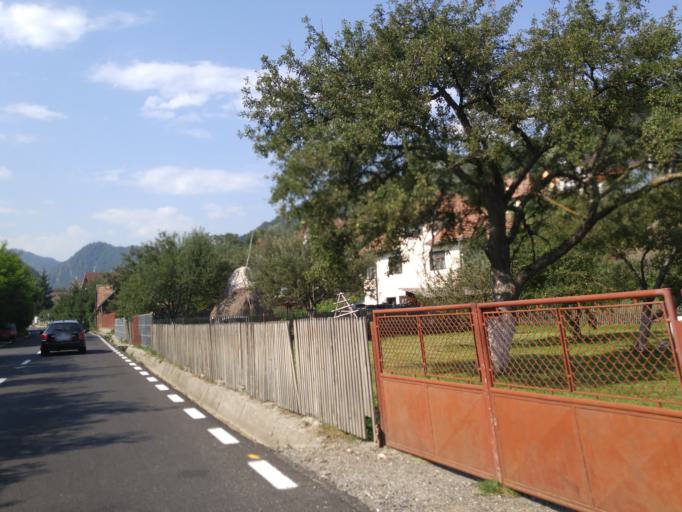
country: RO
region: Brasov
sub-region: Municipiul Brasov
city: Moeciu de Jos
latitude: 45.4863
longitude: 25.3222
